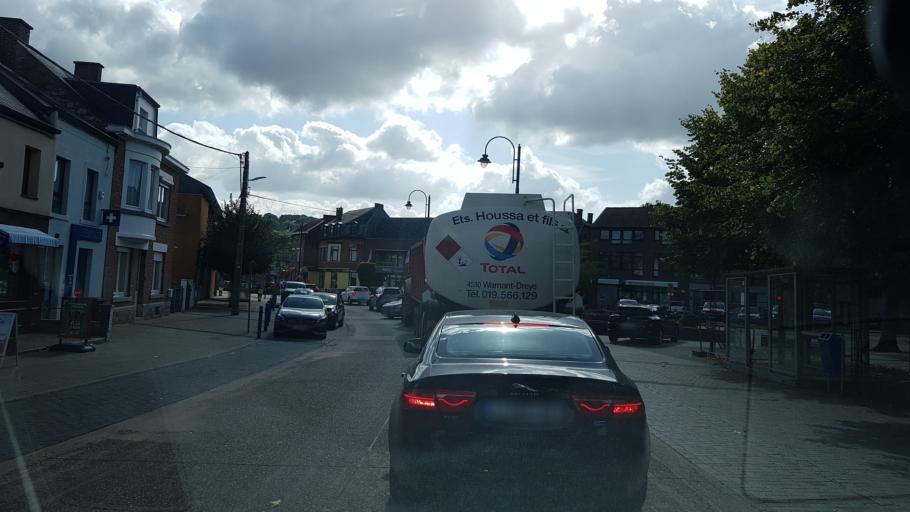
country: BE
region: Wallonia
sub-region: Province de Liege
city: Wanze
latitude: 50.5363
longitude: 5.2154
